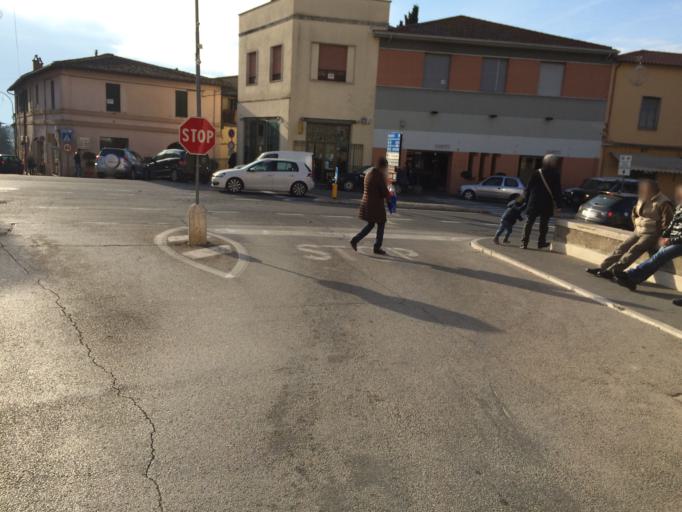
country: IT
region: Umbria
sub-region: Provincia di Terni
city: Amelia
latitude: 42.5537
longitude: 12.4168
